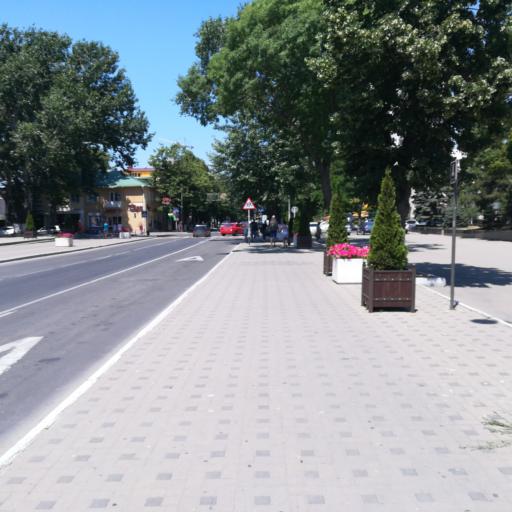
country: RU
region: Krasnodarskiy
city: Anapa
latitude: 44.8928
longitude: 37.3098
